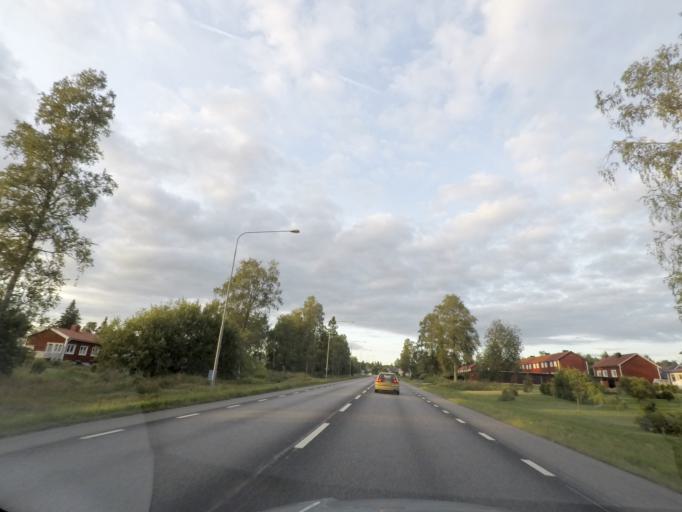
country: SE
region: OErebro
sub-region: Hallefors Kommun
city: Haellefors
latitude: 59.7795
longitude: 14.5286
